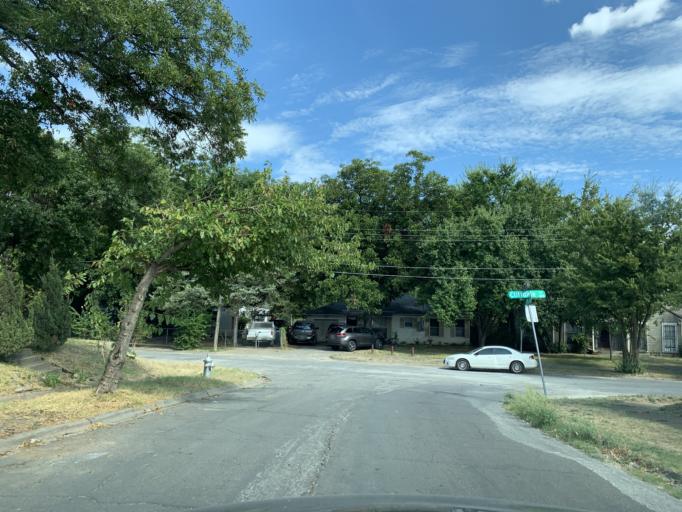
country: US
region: Texas
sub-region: Dallas County
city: Cockrell Hill
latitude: 32.7480
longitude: -96.8666
